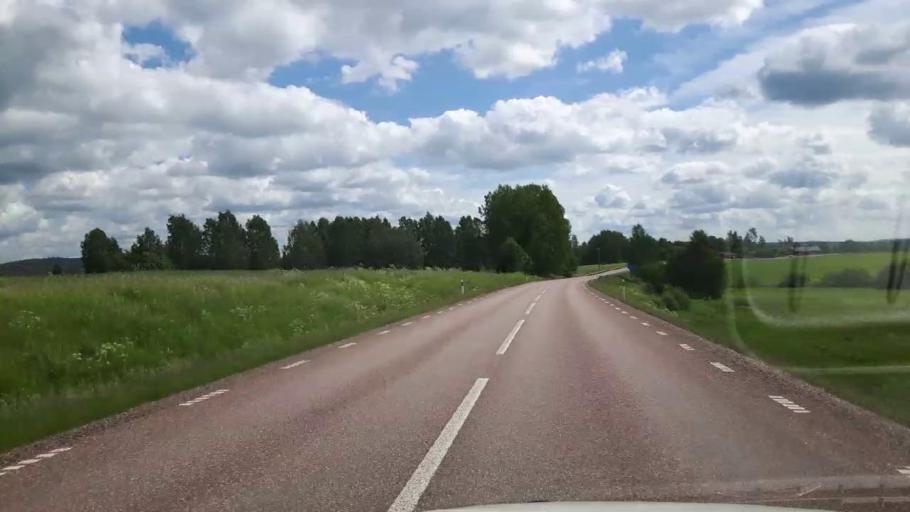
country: SE
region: Dalarna
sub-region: Saters Kommun
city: Saeter
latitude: 60.4069
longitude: 15.8668
